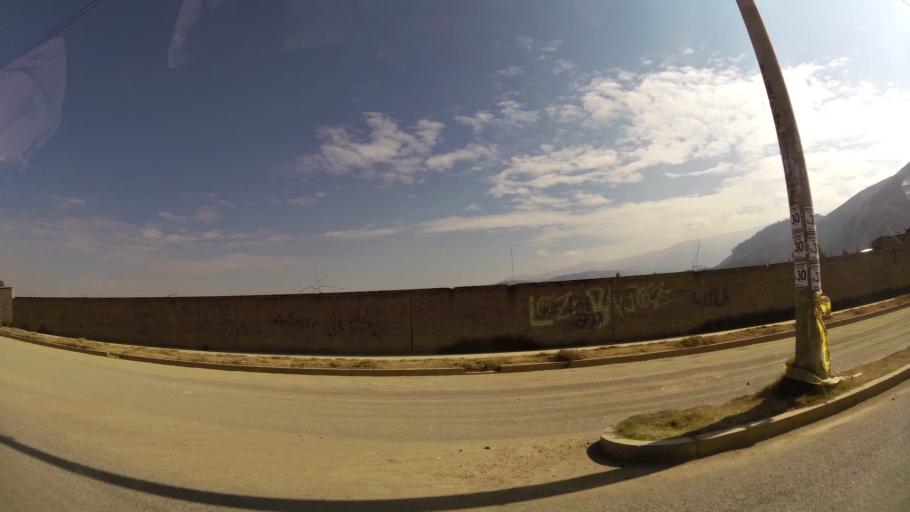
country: PE
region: Junin
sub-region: Provincia de Huancayo
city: Huancayo
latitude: -12.0575
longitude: -75.1892
